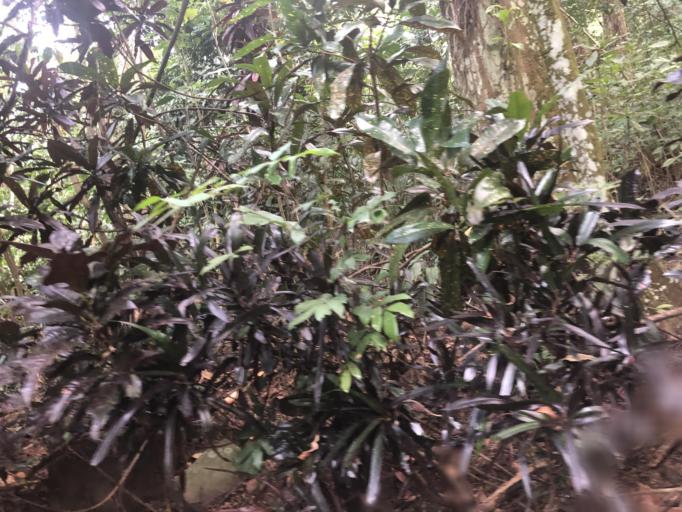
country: TW
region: Taiwan
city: Yujing
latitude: 22.9328
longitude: 120.5924
